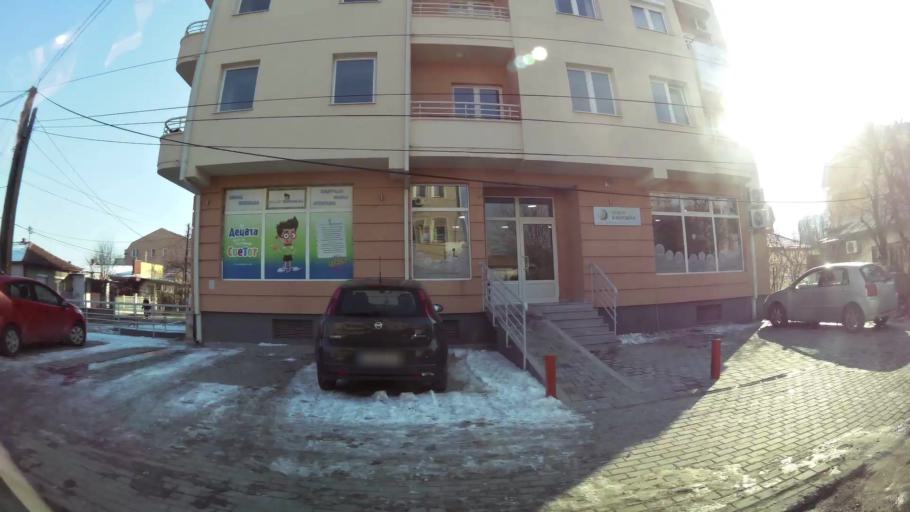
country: MK
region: Karpos
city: Skopje
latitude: 41.9842
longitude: 21.4406
